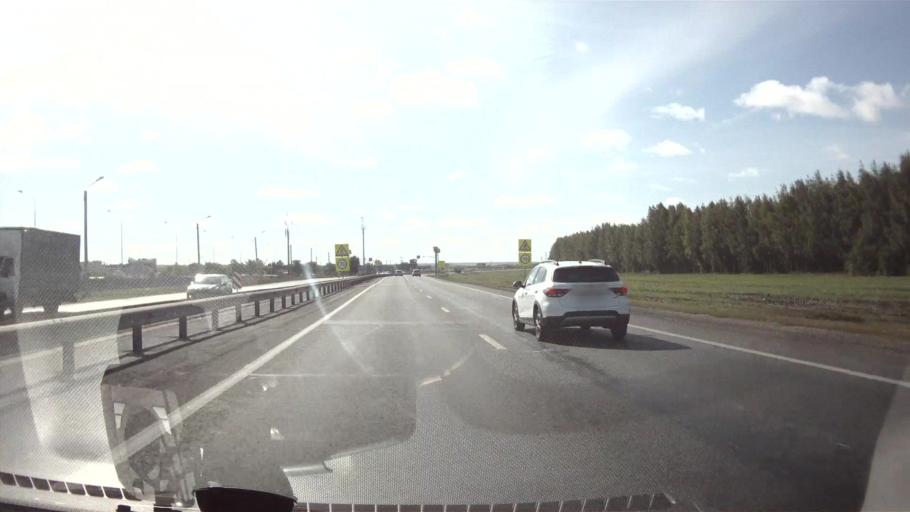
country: RU
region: Ulyanovsk
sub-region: Ulyanovskiy Rayon
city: Ulyanovsk
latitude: 54.2779
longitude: 48.2595
